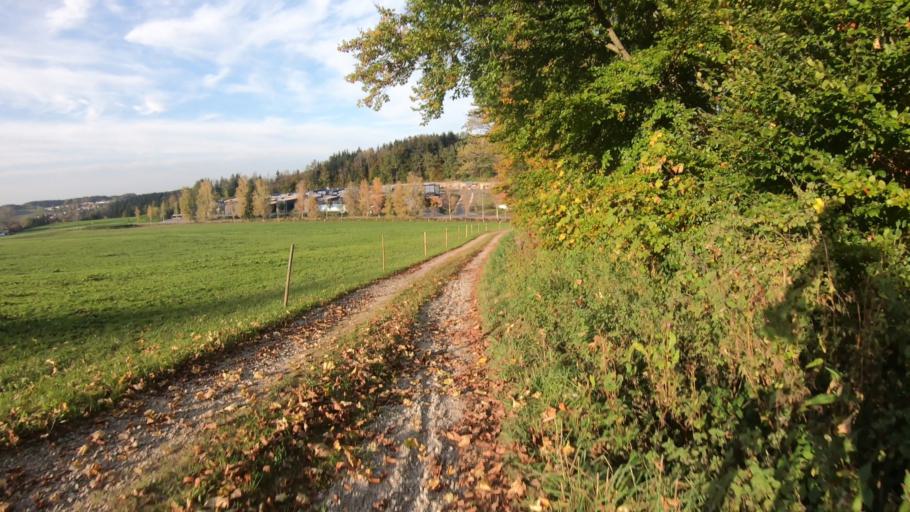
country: DE
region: Bavaria
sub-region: Upper Bavaria
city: Bergen
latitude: 47.8104
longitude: 12.6079
